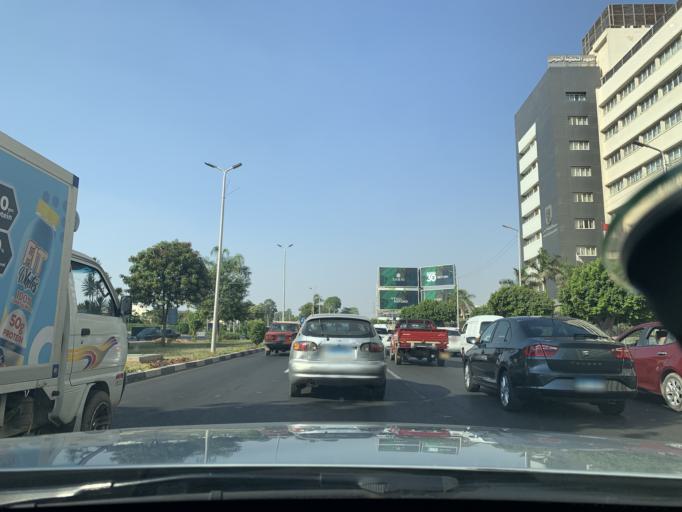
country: EG
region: Muhafazat al Qahirah
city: Cairo
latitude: 30.0798
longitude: 31.3159
